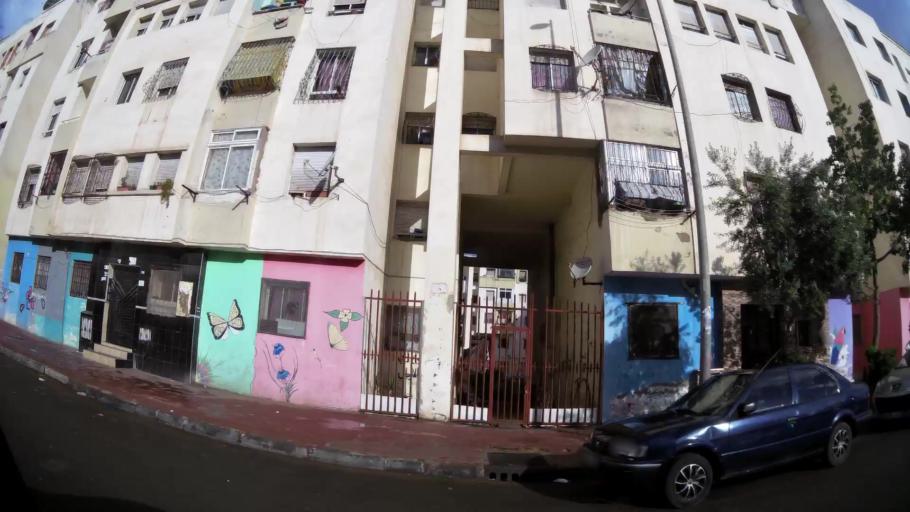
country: MA
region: Grand Casablanca
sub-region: Mediouna
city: Tit Mellil
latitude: 33.5954
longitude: -7.5355
